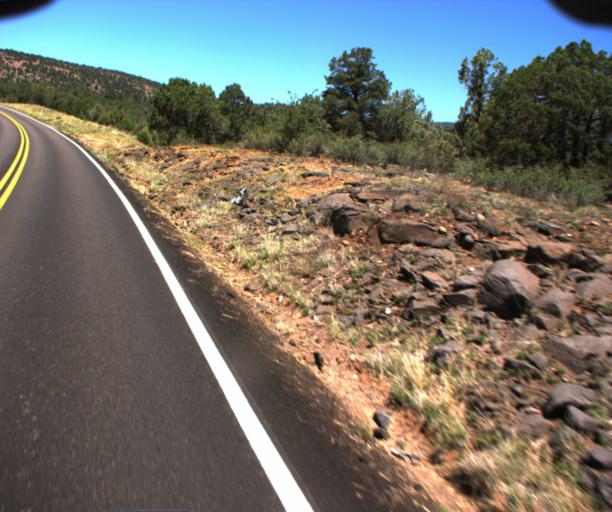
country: US
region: Arizona
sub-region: Gila County
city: Pine
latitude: 34.3394
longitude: -111.4224
